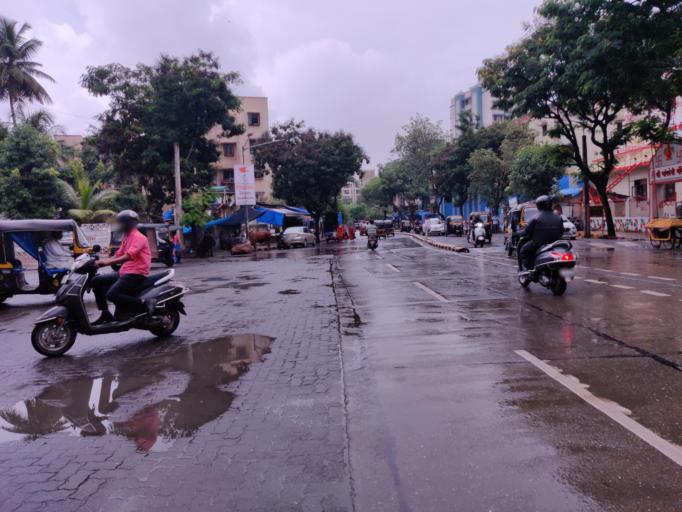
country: IN
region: Maharashtra
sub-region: Mumbai Suburban
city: Borivli
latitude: 19.2552
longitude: 72.8606
